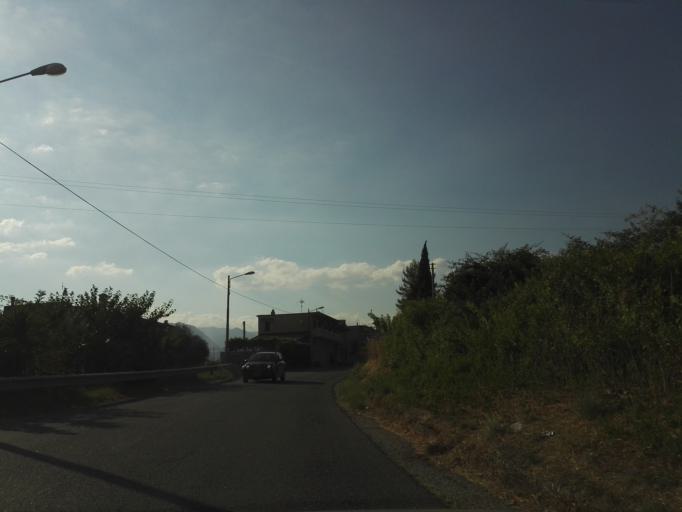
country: IT
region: Calabria
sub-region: Provincia di Reggio Calabria
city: Monasterace
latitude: 38.4459
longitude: 16.5354
